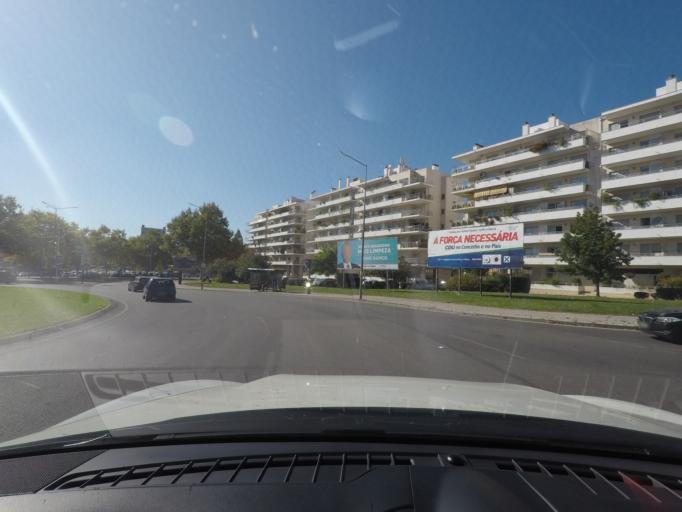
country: PT
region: Coimbra
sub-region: Coimbra
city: Coimbra
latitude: 40.1945
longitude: -8.4058
